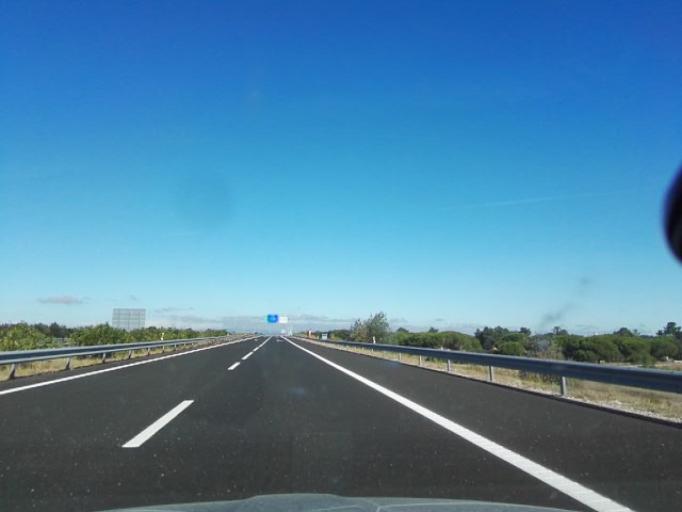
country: PT
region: Santarem
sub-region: Benavente
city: Benavente
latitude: 38.9491
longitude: -8.8223
